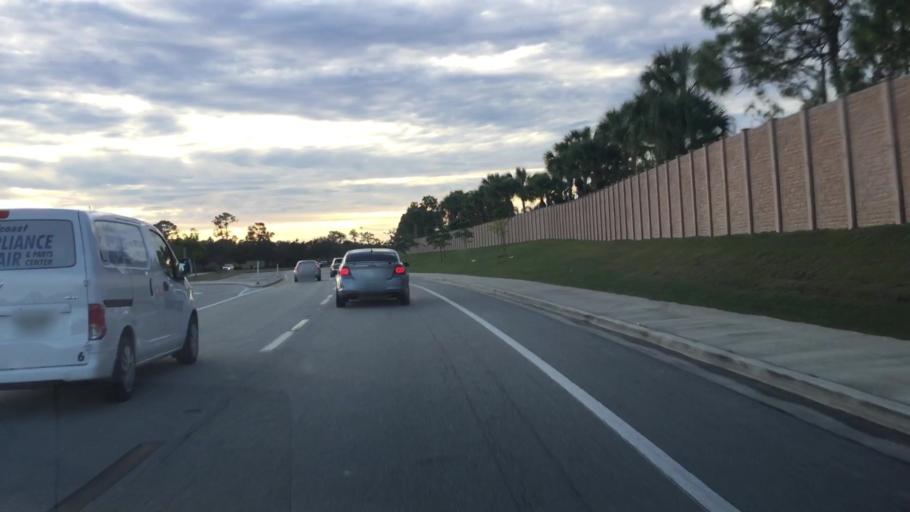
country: US
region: Florida
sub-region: Lee County
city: Gateway
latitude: 26.5947
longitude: -81.7857
